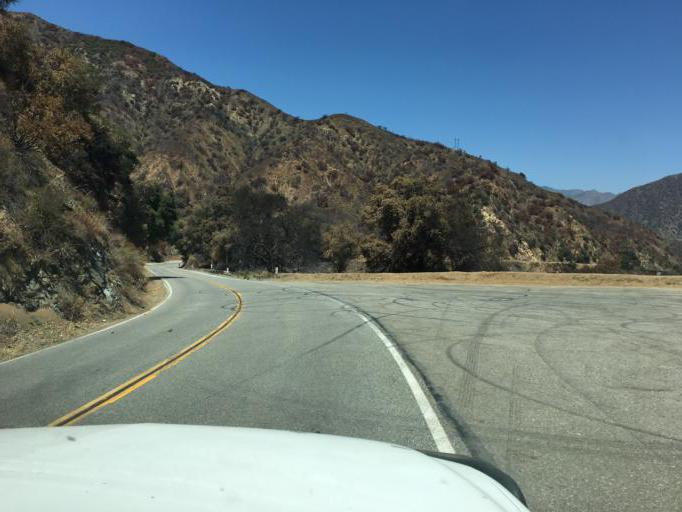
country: US
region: California
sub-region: Los Angeles County
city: Glendora
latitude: 34.1852
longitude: -117.8718
